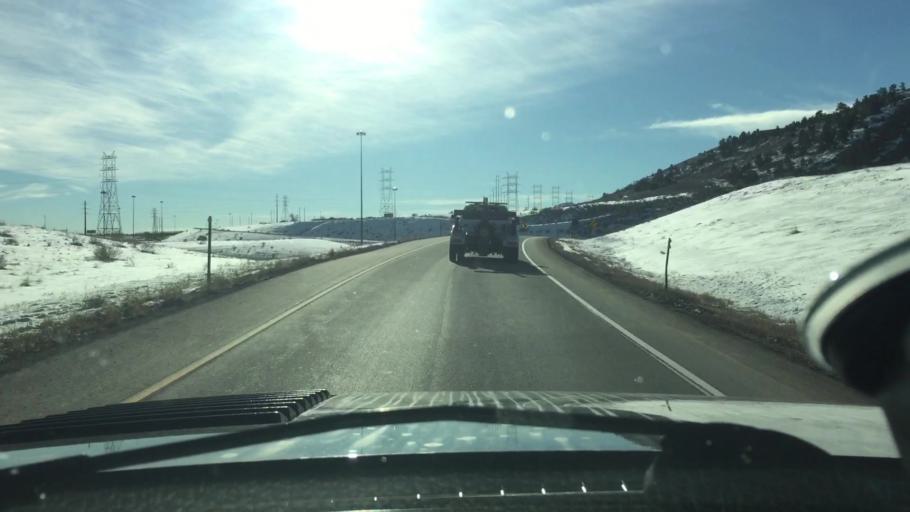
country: US
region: Colorado
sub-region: Jefferson County
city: Indian Hills
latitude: 39.6386
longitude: -105.1703
